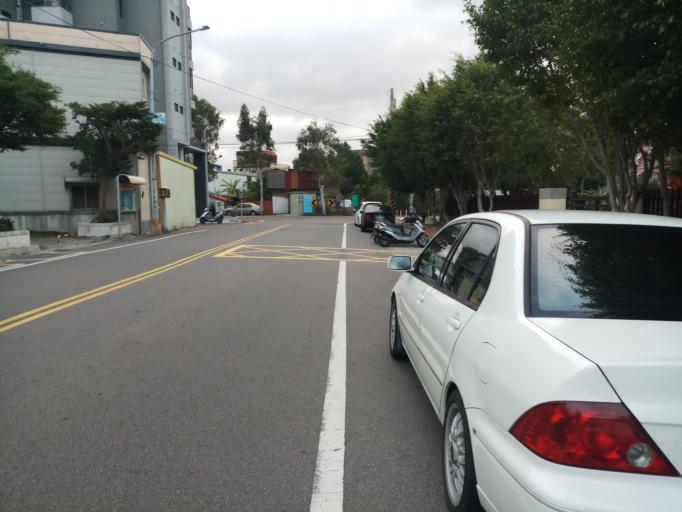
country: TW
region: Taiwan
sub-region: Miaoli
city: Miaoli
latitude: 24.6755
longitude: 120.8620
